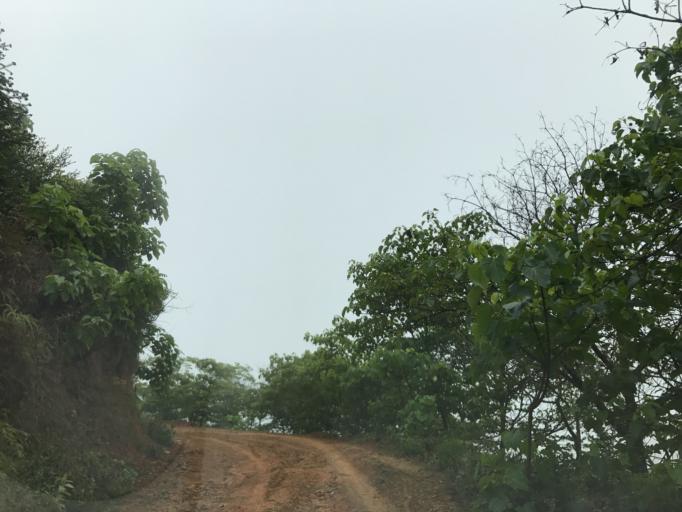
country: CN
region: Guangxi Zhuangzu Zizhiqu
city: Leli
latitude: 24.8053
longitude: 106.0783
